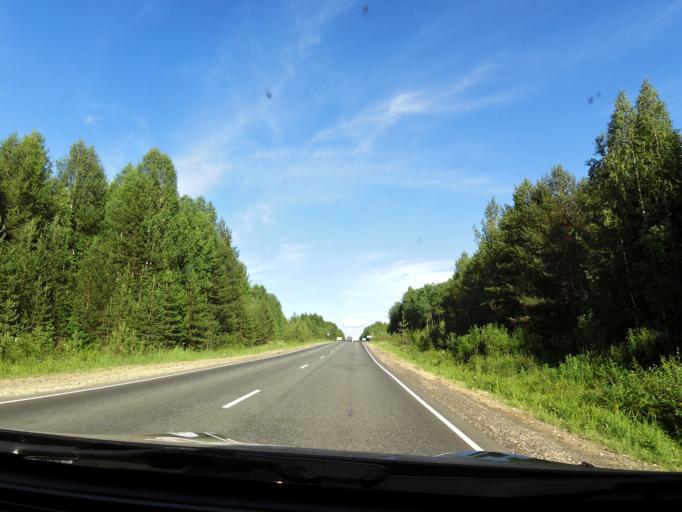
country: RU
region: Kirov
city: Chernaya Kholunitsa
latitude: 58.8705
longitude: 51.5393
